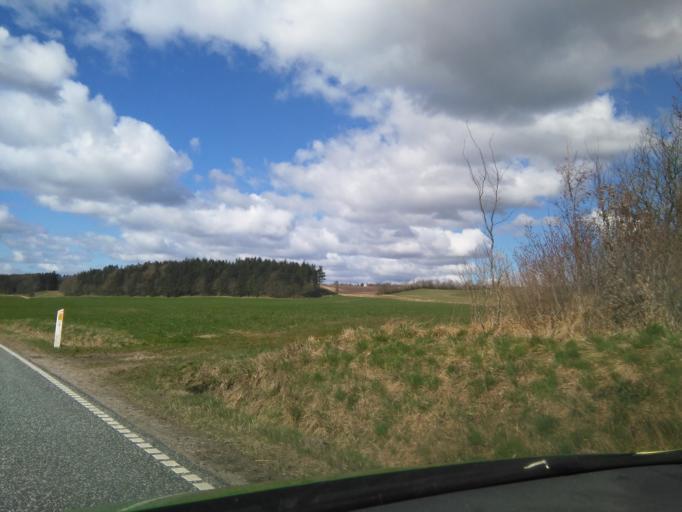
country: DK
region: Central Jutland
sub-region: Horsens Kommune
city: Braedstrup
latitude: 56.0253
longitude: 9.5634
